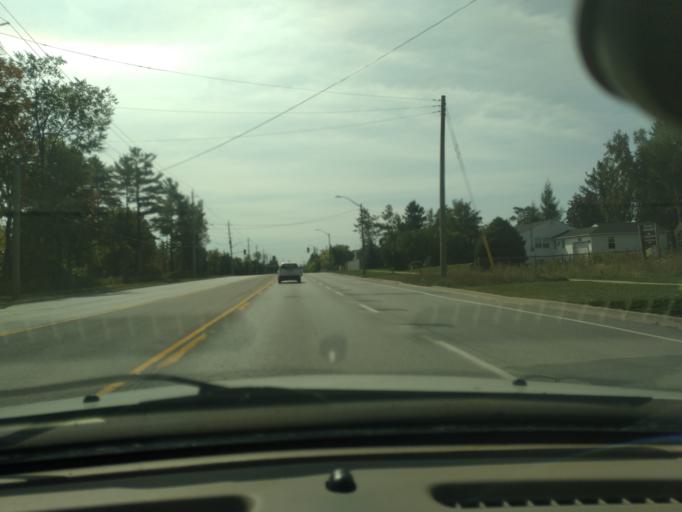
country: CA
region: Ontario
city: Barrie
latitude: 44.3435
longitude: -79.7016
